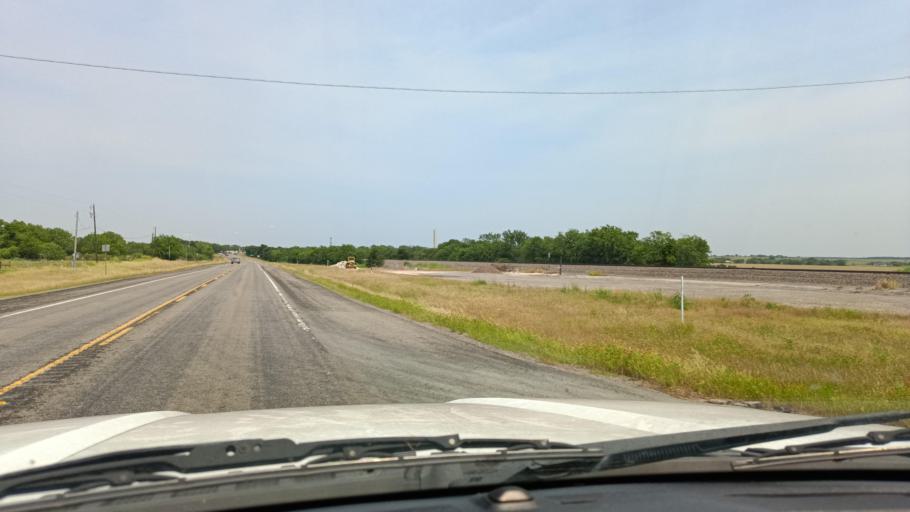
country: US
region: Texas
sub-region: Bell County
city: Rogers
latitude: 30.8765
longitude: -97.1370
